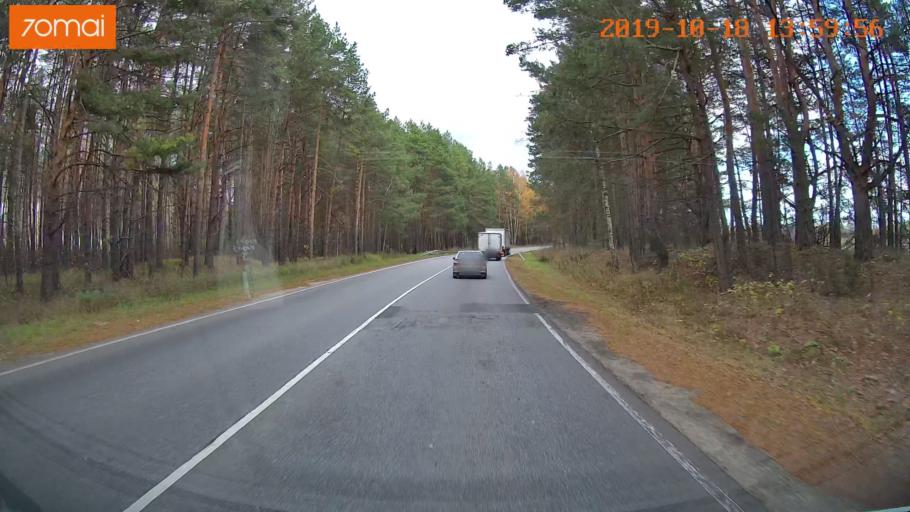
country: RU
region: Rjazan
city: Spas-Klepiki
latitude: 55.0986
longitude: 40.0689
